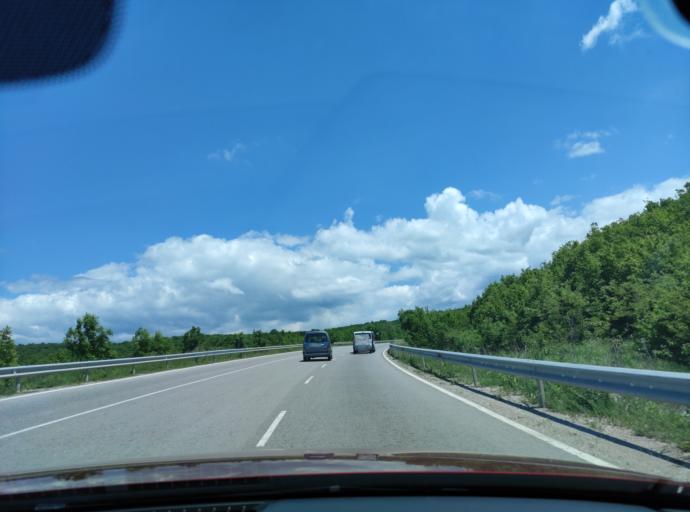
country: BG
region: Sofiya
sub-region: Obshtina Kostinbrod
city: Kostinbrod
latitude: 42.8984
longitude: 23.1527
